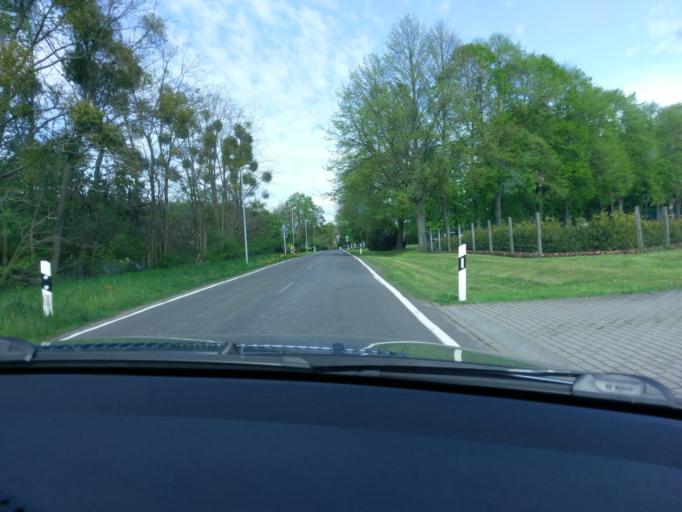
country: DE
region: Brandenburg
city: Hohenfinow
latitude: 52.7564
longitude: 13.8761
